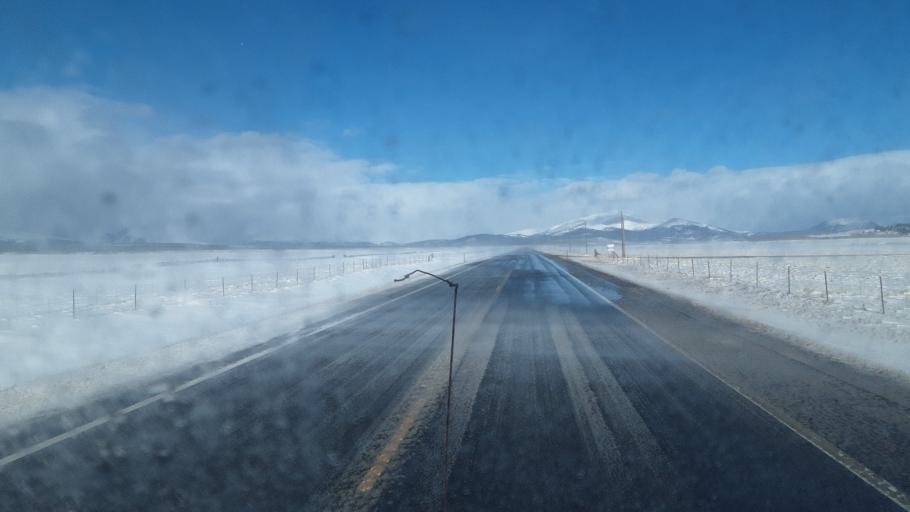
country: US
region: Colorado
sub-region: Park County
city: Fairplay
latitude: 39.1570
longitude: -105.9997
